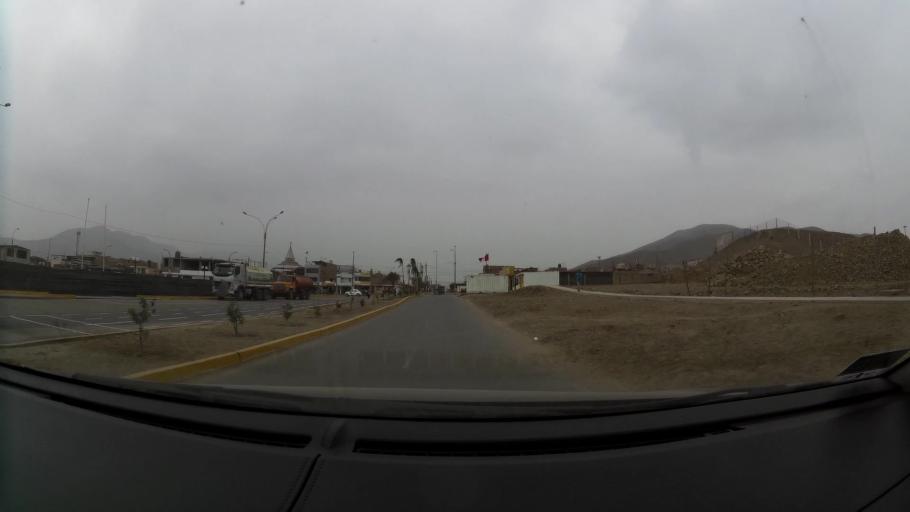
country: PE
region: Lima
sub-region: Lima
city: Santa Rosa
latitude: -11.7865
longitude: -77.1577
